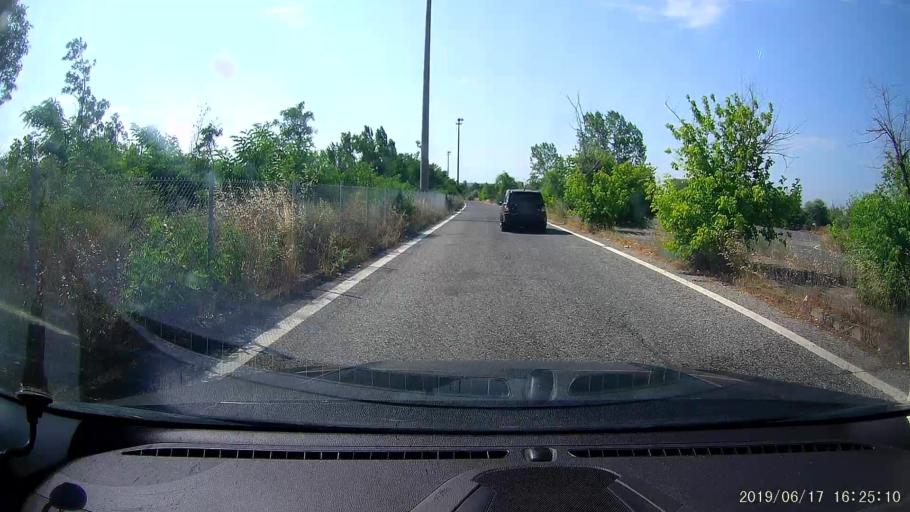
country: TR
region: Tekirdag
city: Marmaracik
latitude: 41.2903
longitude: 27.7830
